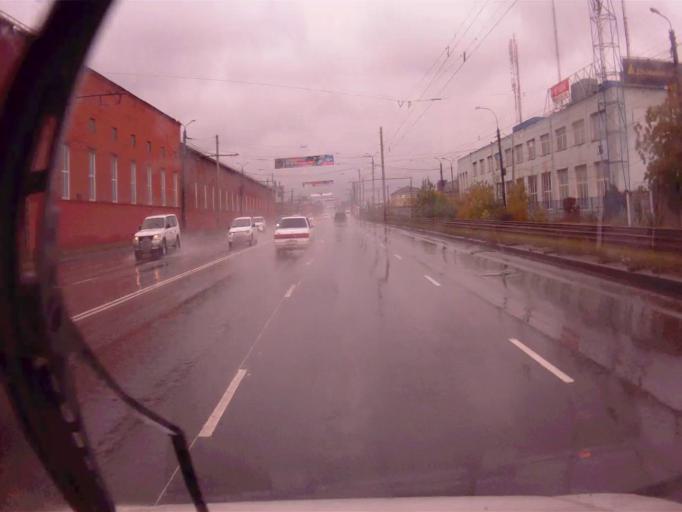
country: RU
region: Chelyabinsk
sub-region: Gorod Chelyabinsk
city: Chelyabinsk
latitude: 55.2076
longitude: 61.3843
